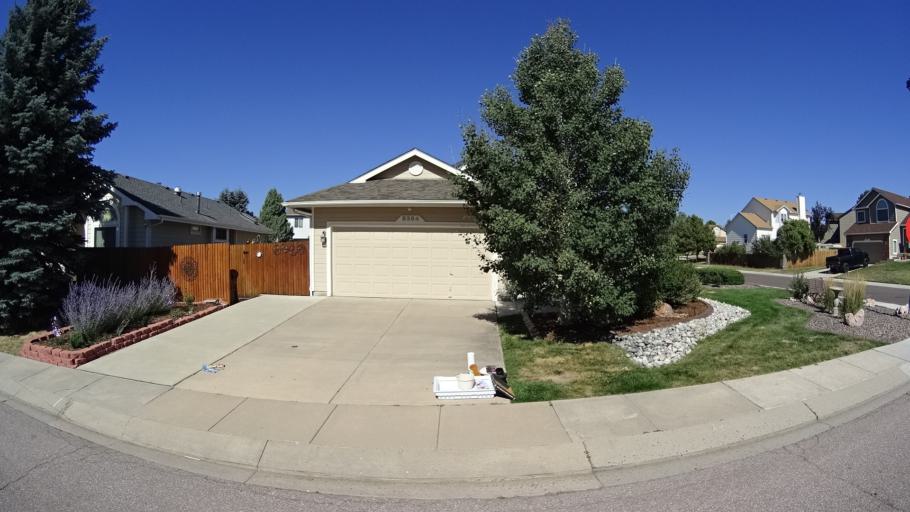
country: US
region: Colorado
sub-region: El Paso County
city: Black Forest
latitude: 38.9532
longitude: -104.7325
